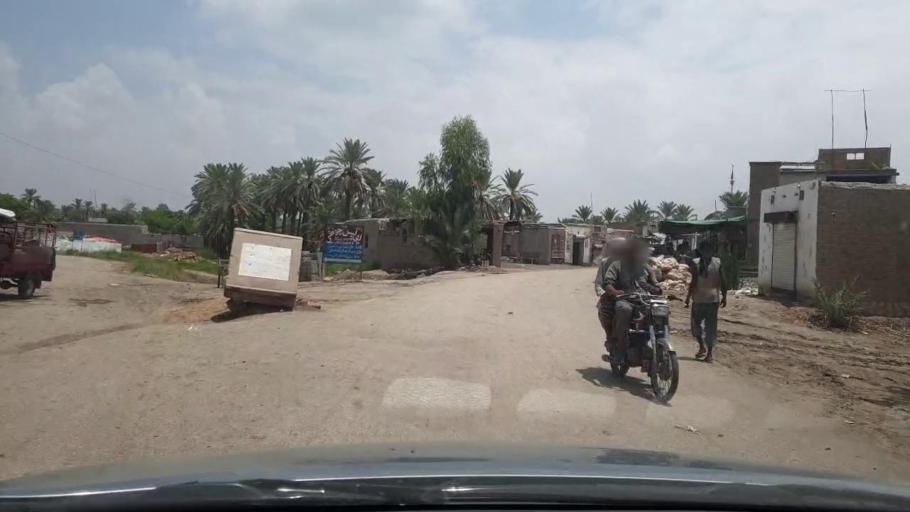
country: PK
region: Sindh
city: Khairpur
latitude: 27.4366
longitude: 68.7658
